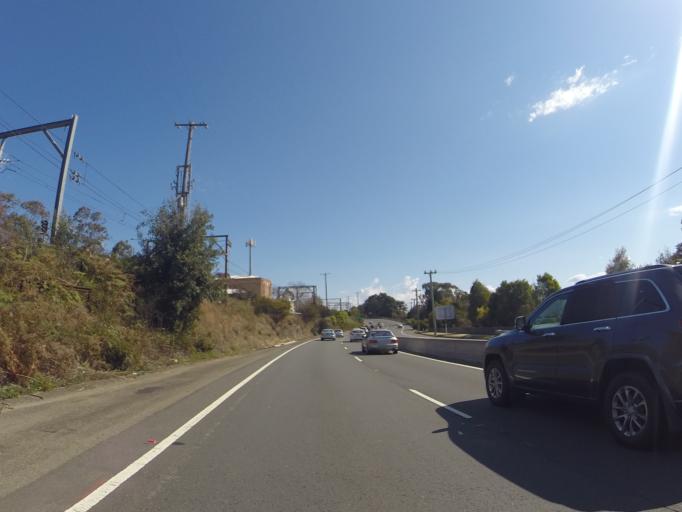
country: AU
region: New South Wales
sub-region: Blue Mountains Municipality
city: Blaxland
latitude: -33.6981
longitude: 150.5684
